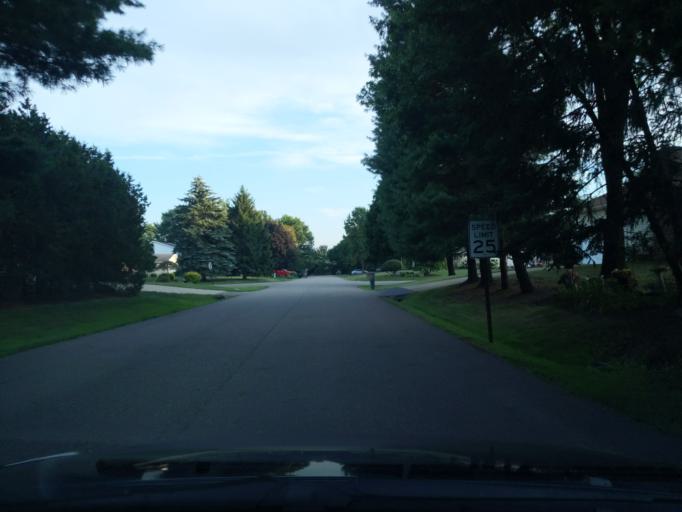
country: US
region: Ohio
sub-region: Stark County
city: Greentown
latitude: 40.9161
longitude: -81.3860
